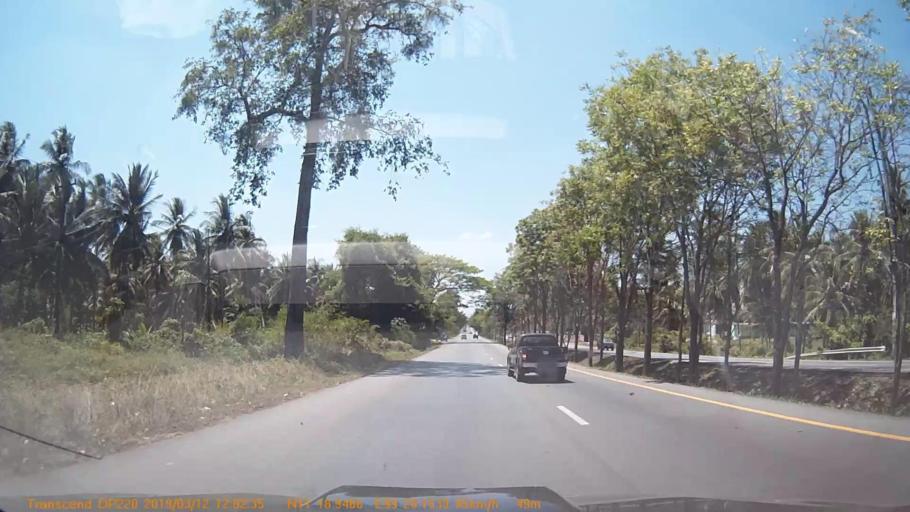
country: TH
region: Prachuap Khiri Khan
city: Bang Saphan
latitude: 11.3158
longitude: 99.4692
